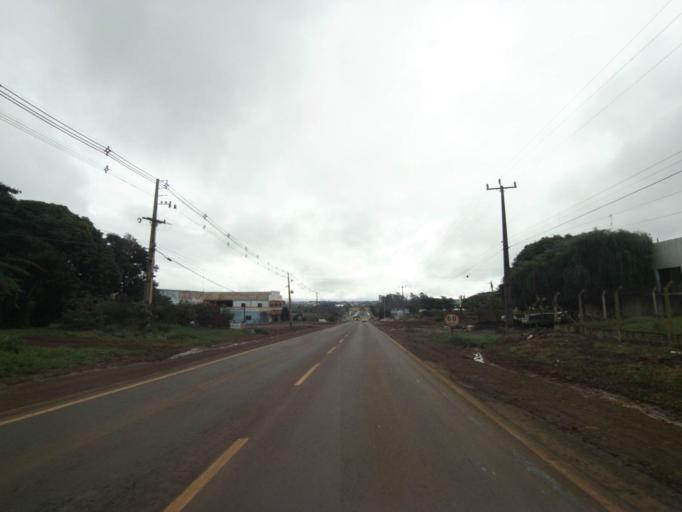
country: BR
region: Parana
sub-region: Marechal Candido Rondon
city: Marechal Candido Rondon
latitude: -24.5684
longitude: -54.0296
